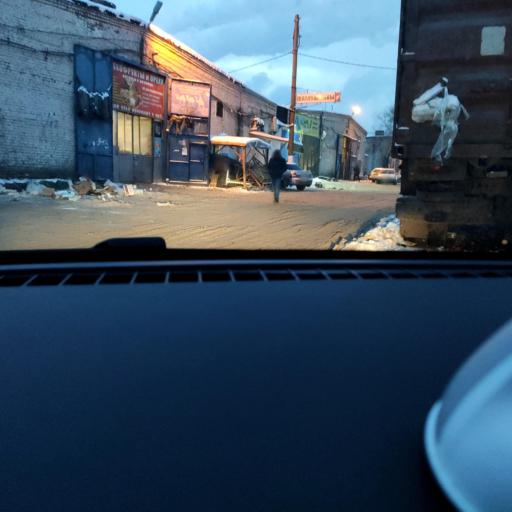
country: RU
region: Samara
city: Petra-Dubrava
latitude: 53.2535
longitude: 50.2922
